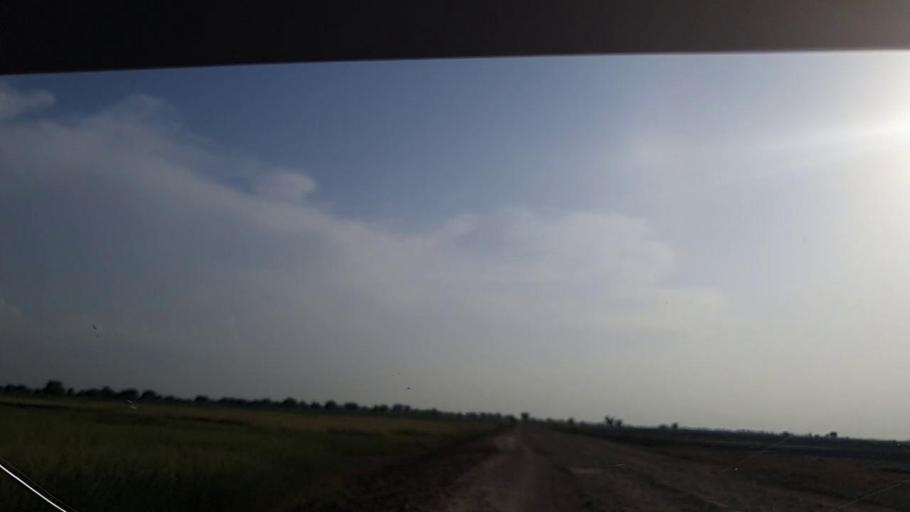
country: PK
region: Sindh
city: Khanpur
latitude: 27.8349
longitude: 69.3684
